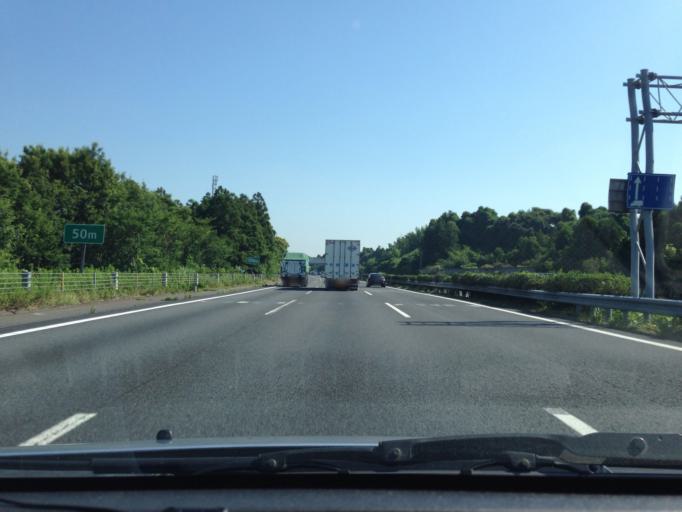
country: JP
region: Ibaraki
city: Ishioka
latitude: 36.1920
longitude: 140.2580
